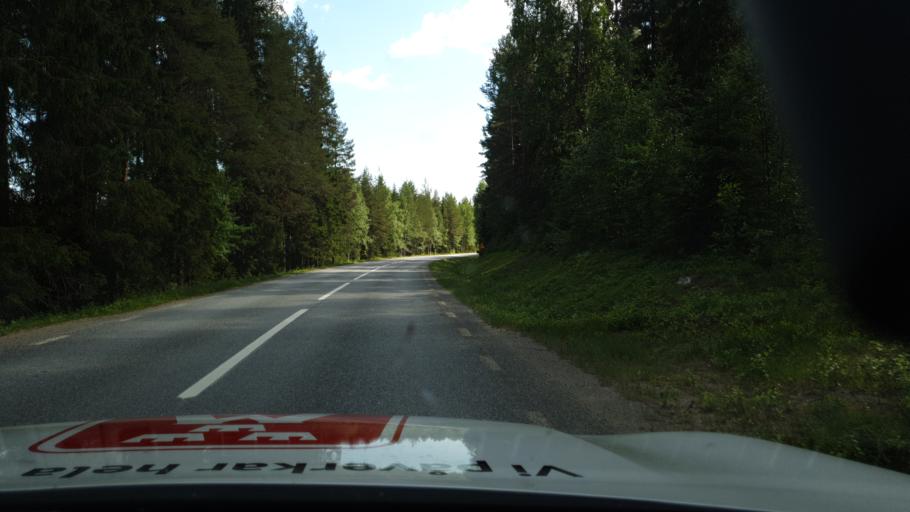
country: SE
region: Vaesterbotten
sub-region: Skelleftea Kommun
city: Burtraesk
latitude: 64.4359
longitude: 20.3992
